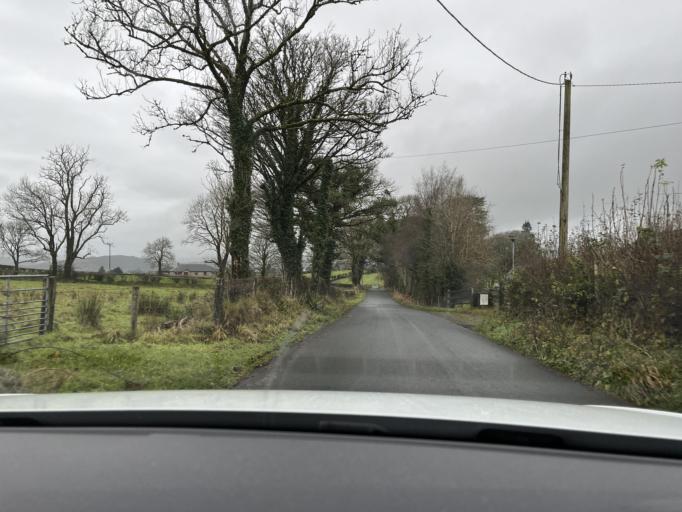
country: IE
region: Connaught
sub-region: County Leitrim
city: Manorhamilton
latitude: 54.3007
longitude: -8.1526
